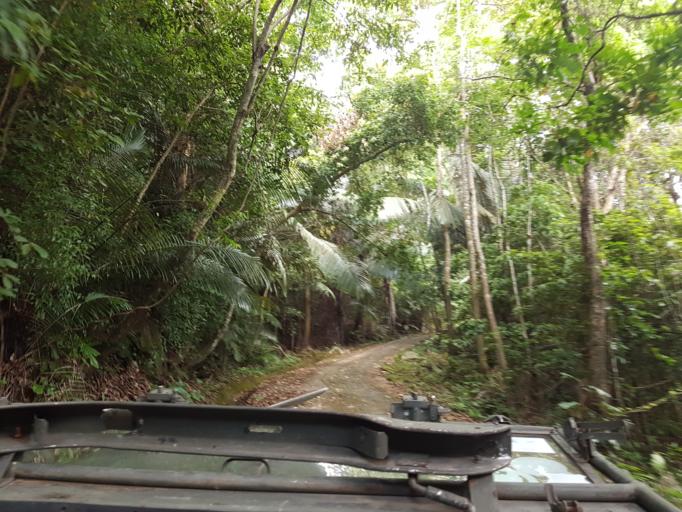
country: TH
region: Pattani
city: Khok Pho
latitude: 6.6556
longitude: 101.0989
